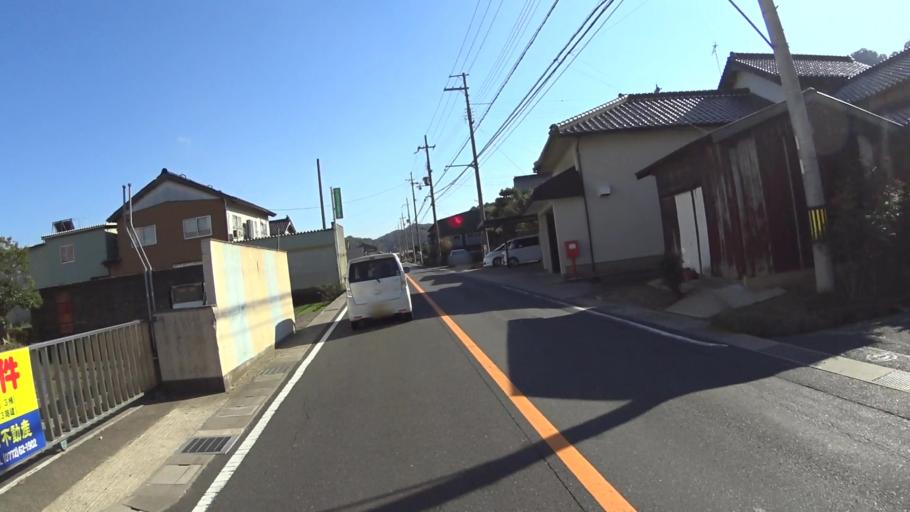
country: JP
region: Kyoto
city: Miyazu
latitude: 35.6596
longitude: 135.0316
